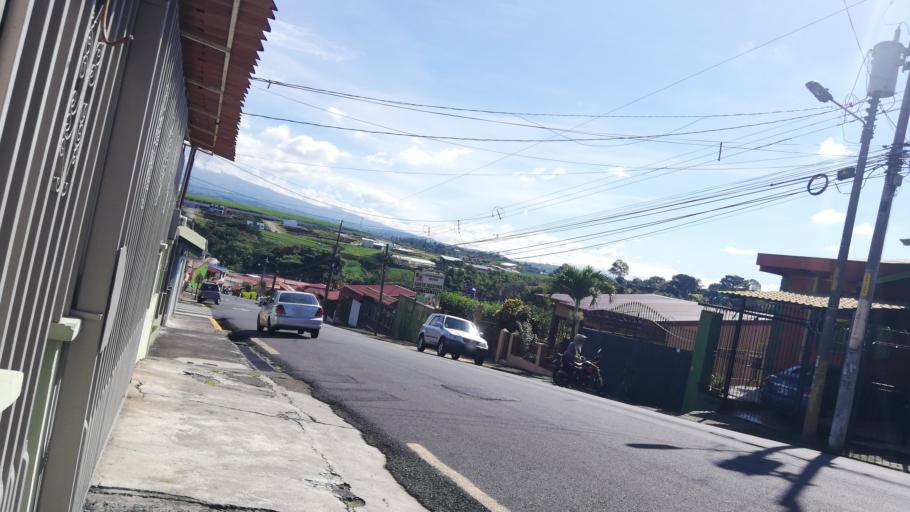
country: CR
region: Alajuela
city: San Juan
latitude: 10.0701
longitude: -84.3093
